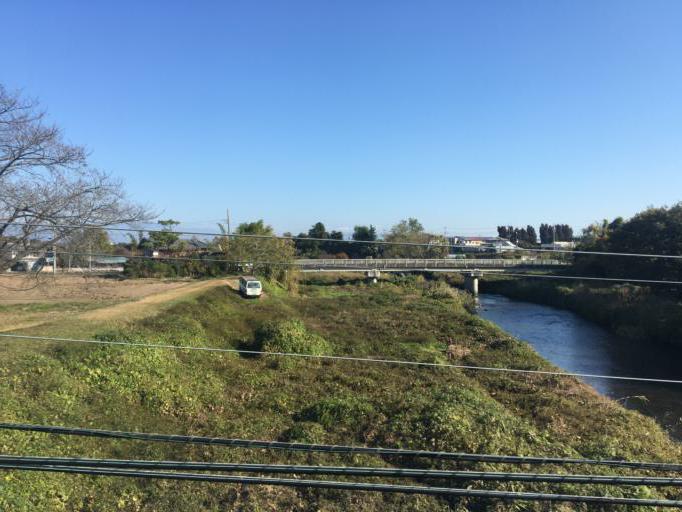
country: JP
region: Gunma
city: Isesaki
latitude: 36.3430
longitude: 139.1643
